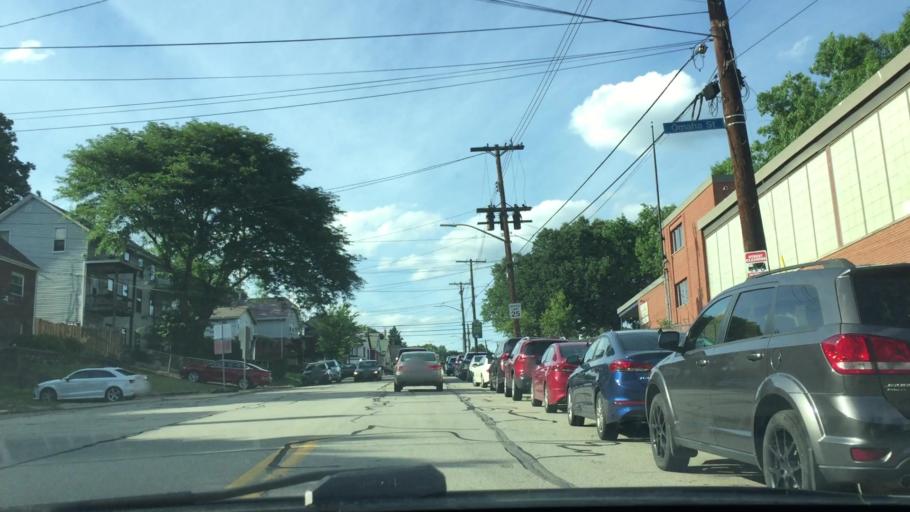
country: US
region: Pennsylvania
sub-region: Allegheny County
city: Pittsburgh
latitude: 40.4307
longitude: -80.0137
